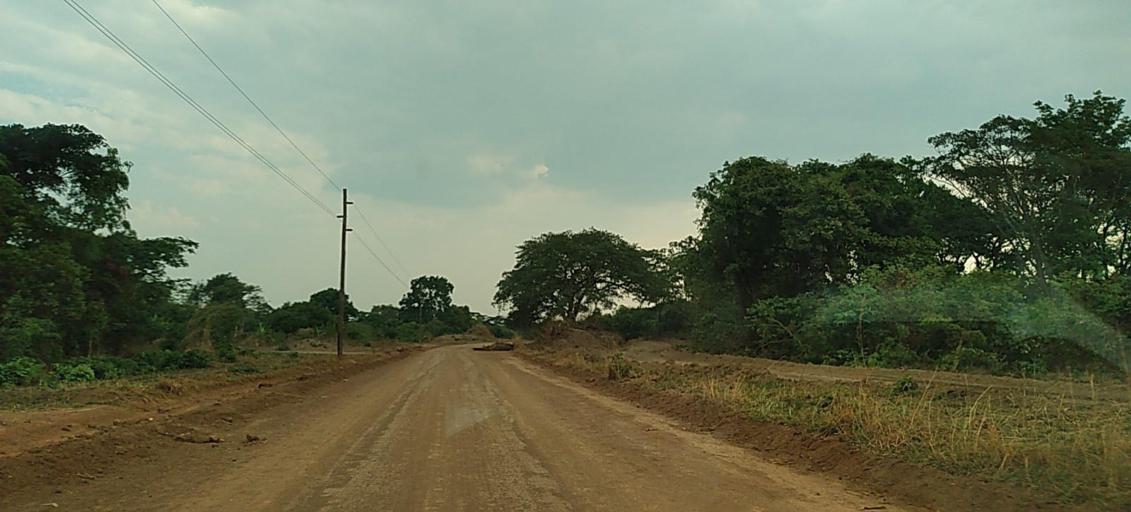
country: ZM
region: Copperbelt
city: Kalulushi
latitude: -12.9133
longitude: 27.9453
